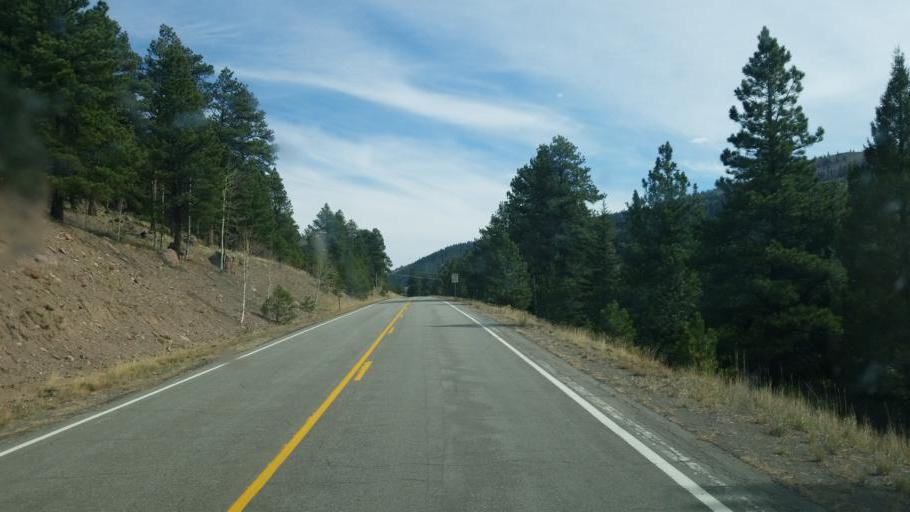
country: US
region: Colorado
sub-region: Conejos County
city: Conejos
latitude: 37.0786
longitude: -106.2931
